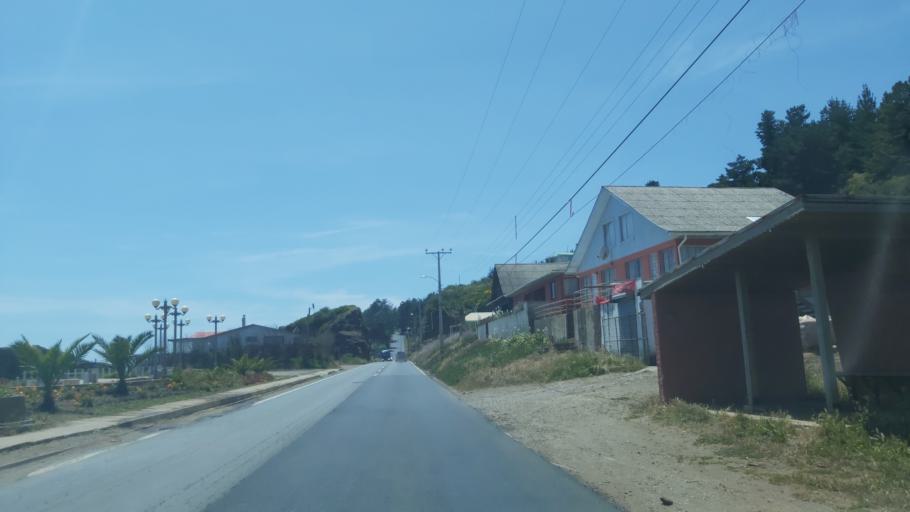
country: CL
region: Maule
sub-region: Provincia de Cauquenes
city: Cauquenes
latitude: -35.8371
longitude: -72.6250
